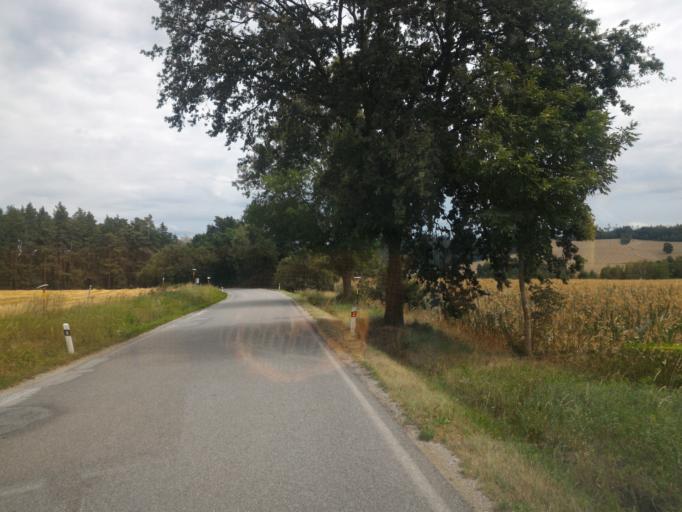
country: CZ
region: Jihocesky
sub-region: Okres Jindrichuv Hradec
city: Dacice
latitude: 49.0930
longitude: 15.4741
